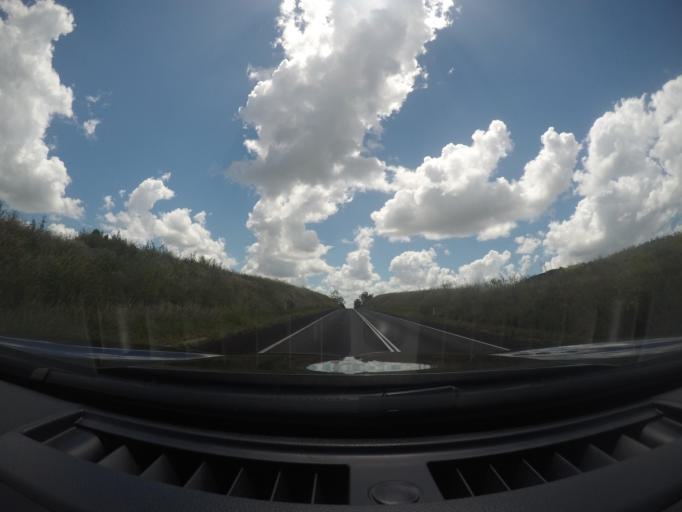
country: AU
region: Queensland
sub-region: Moreton Bay
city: Woodford
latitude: -27.1507
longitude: 152.5416
